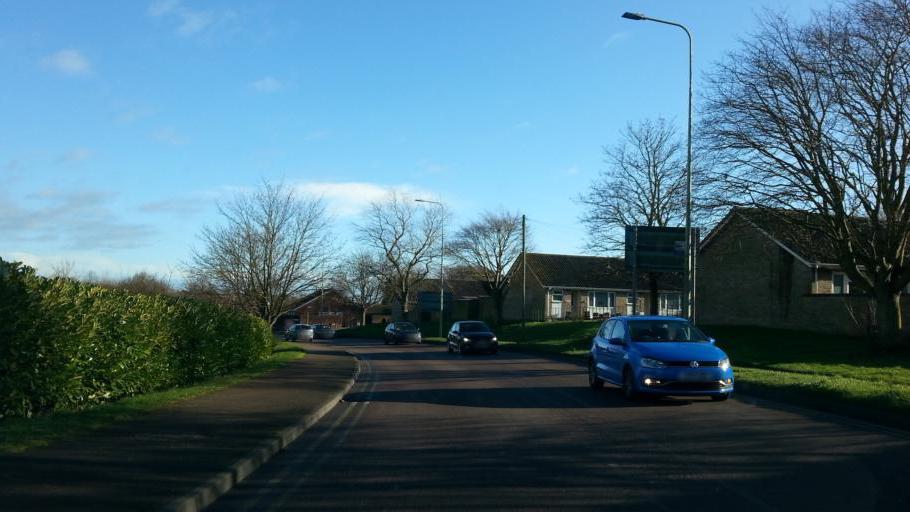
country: GB
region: England
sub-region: Suffolk
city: Halesworth
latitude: 52.3403
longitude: 1.5011
